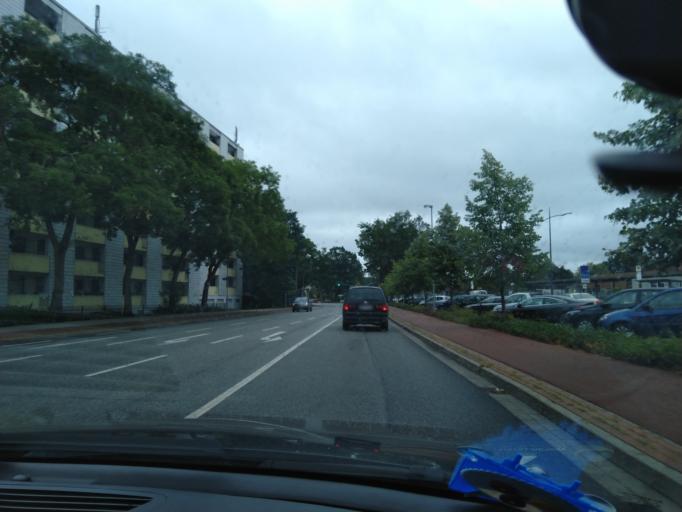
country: DE
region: Lower Saxony
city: Nordhorn
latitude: 52.4308
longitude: 7.0643
